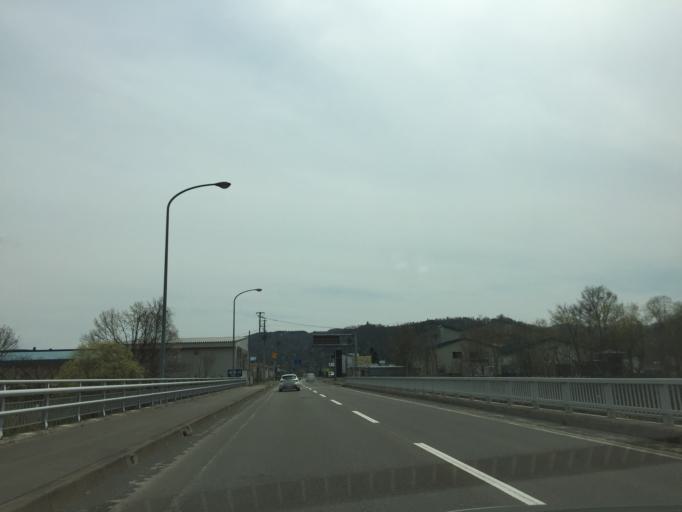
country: JP
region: Hokkaido
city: Ashibetsu
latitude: 43.5333
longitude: 142.1702
